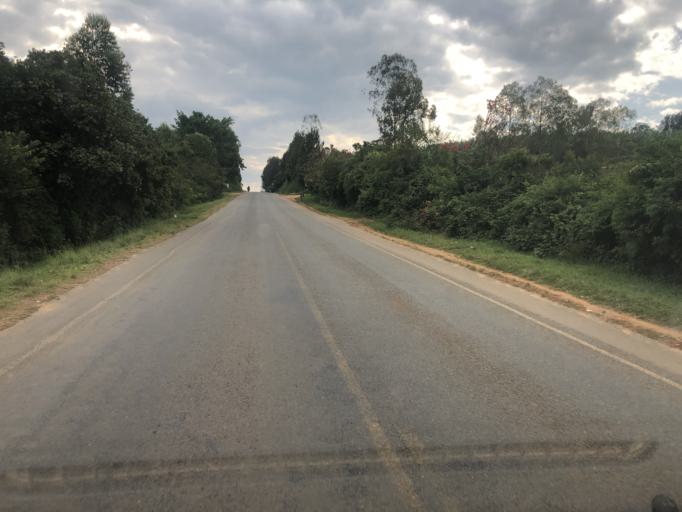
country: UG
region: Western Region
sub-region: Sheema District
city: Kibingo
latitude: -0.5625
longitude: 30.3392
